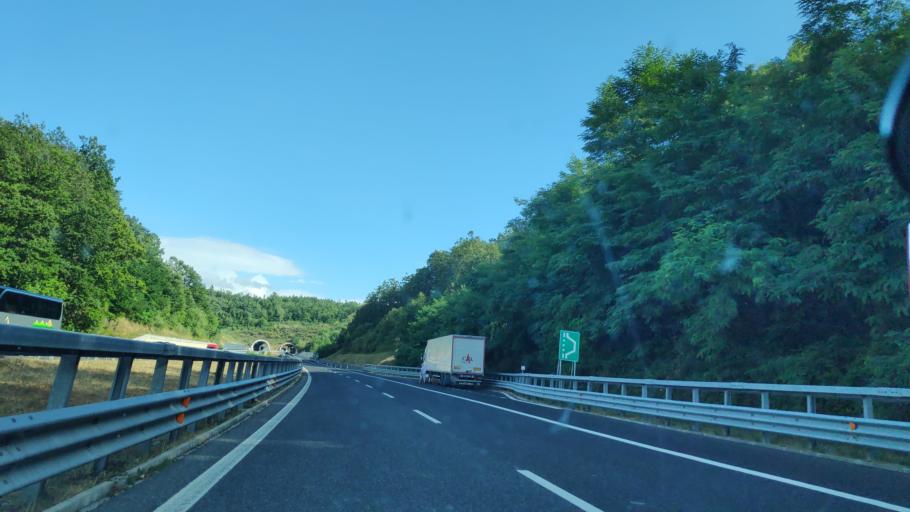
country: IT
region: Campania
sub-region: Provincia di Salerno
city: Casalbuono
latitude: 40.2377
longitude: 15.6607
